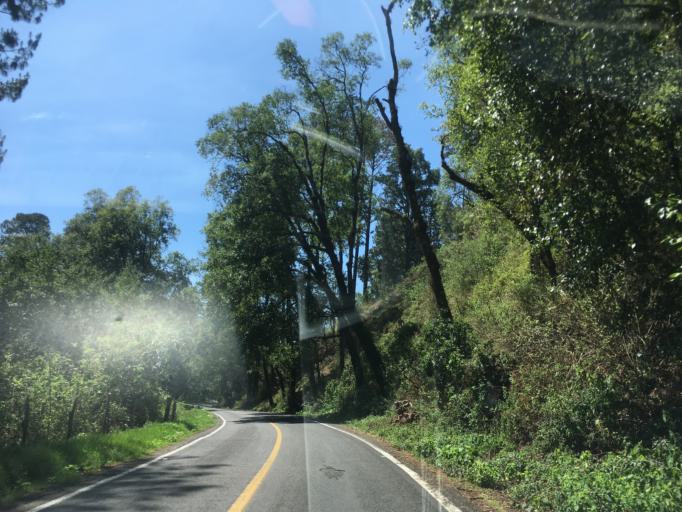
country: MX
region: Michoacan
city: Tzitzio
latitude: 19.6546
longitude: -100.7972
